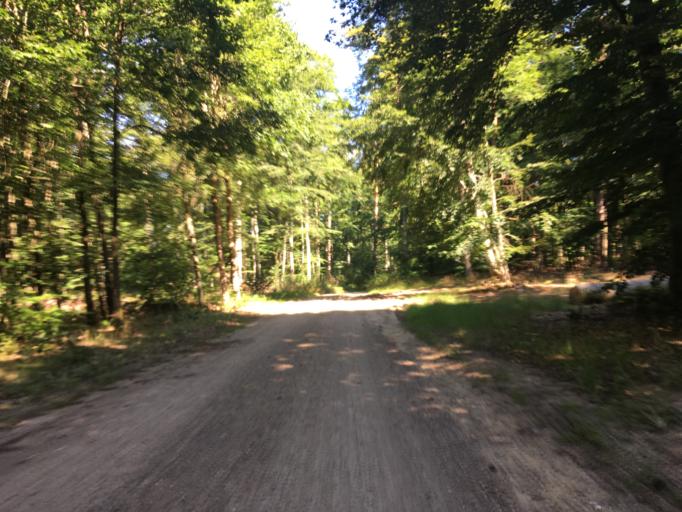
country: DE
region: Brandenburg
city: Furstenberg
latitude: 53.1727
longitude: 13.0518
